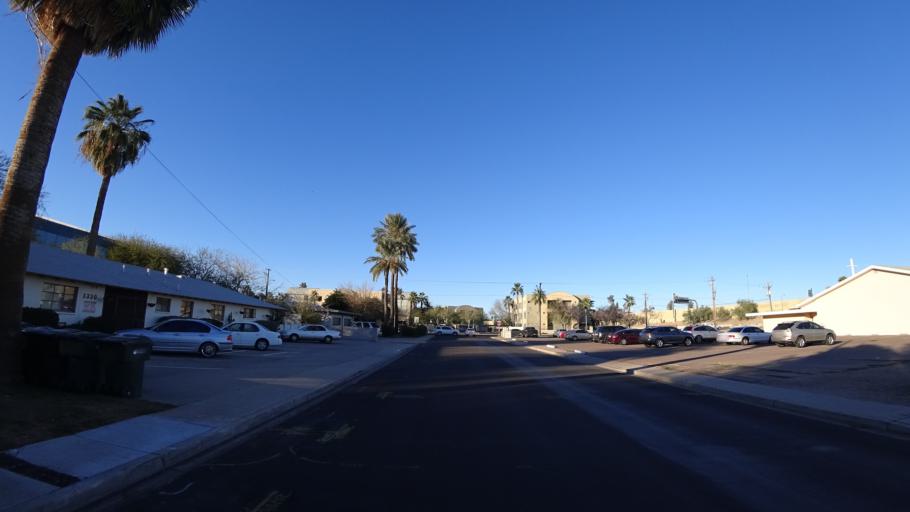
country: US
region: Arizona
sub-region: Maricopa County
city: Phoenix
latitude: 33.4868
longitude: -112.0438
